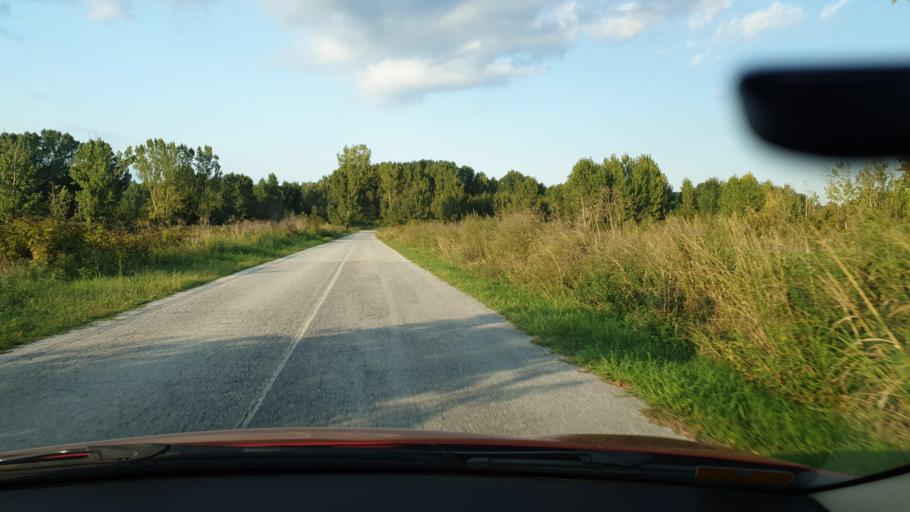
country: GR
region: Central Macedonia
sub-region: Nomos Chalkidikis
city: Galatista
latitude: 40.5590
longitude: 23.3088
